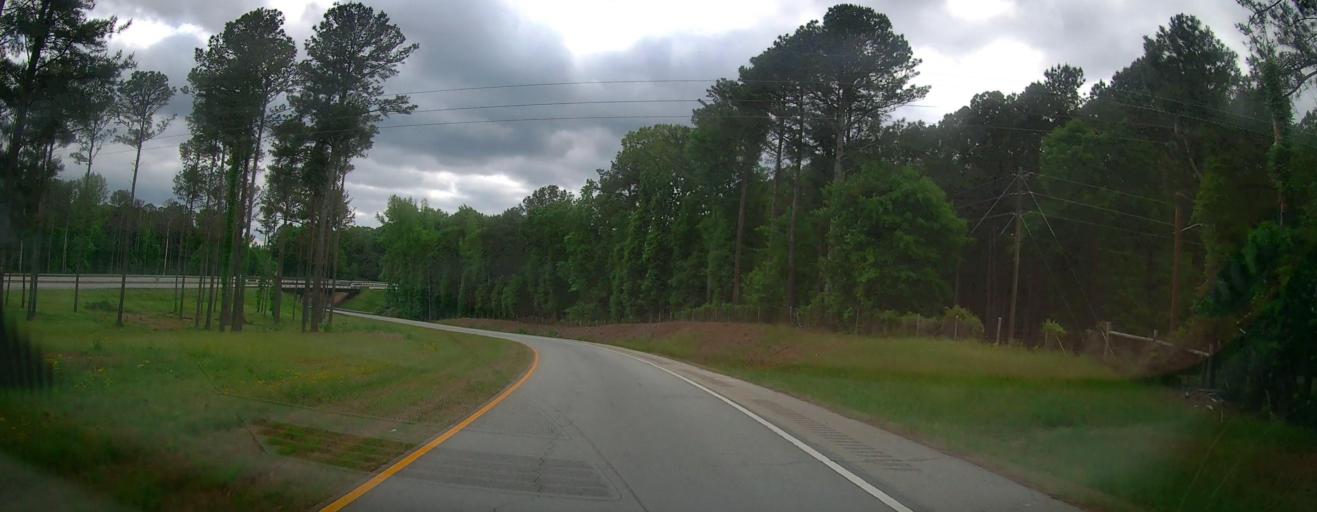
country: US
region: Georgia
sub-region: Walton County
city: Monroe
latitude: 33.8062
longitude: -83.6948
